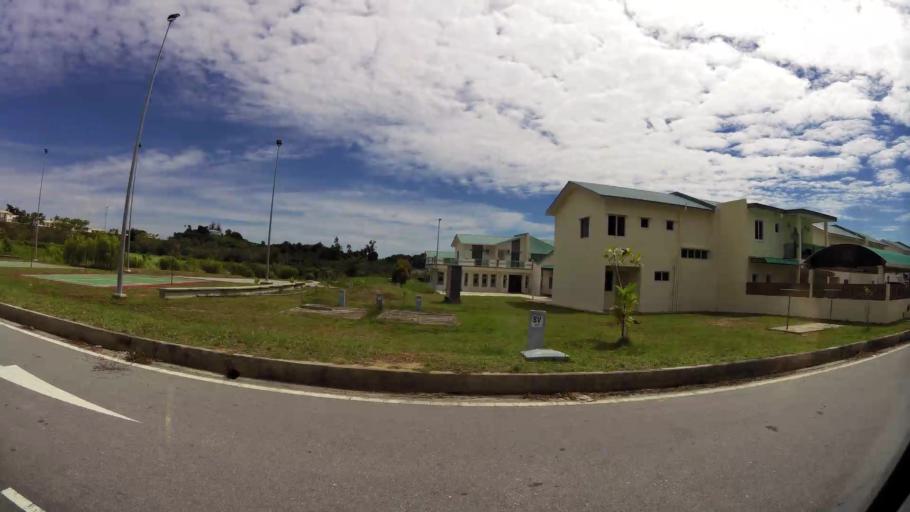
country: BN
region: Brunei and Muara
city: Bandar Seri Begawan
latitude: 4.9842
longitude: 115.0154
